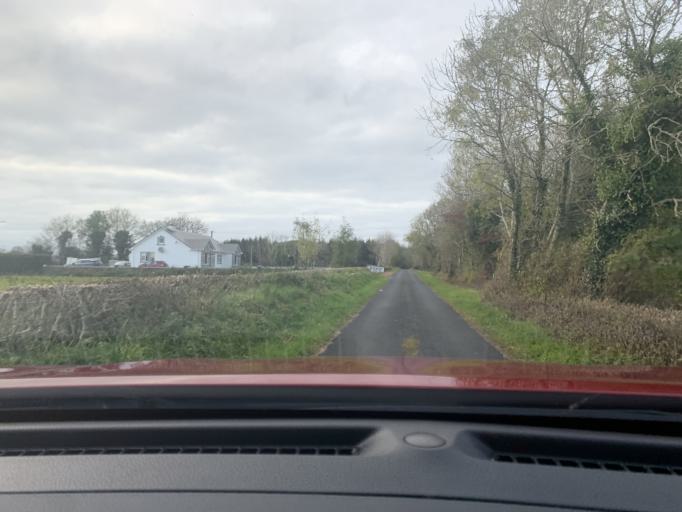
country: IE
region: Connaught
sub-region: Roscommon
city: Ballaghaderreen
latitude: 54.0116
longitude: -8.6089
